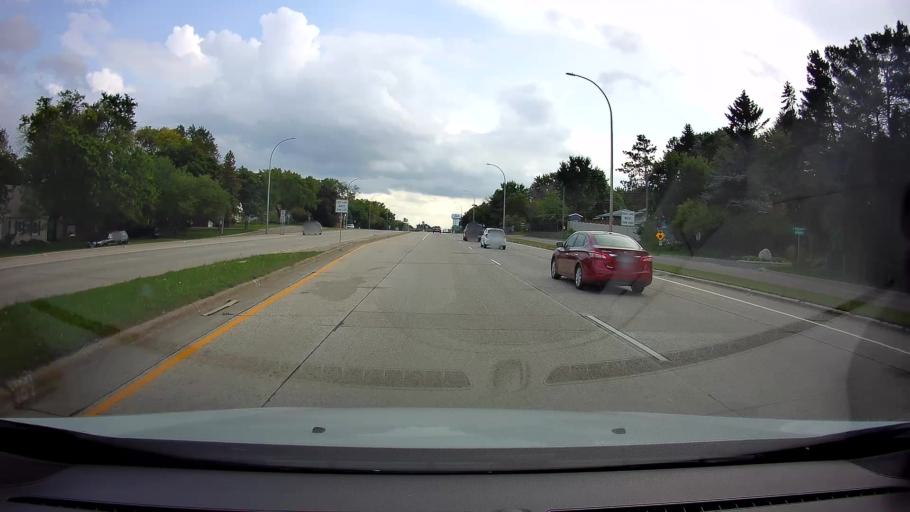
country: US
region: Minnesota
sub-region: Ramsey County
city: Falcon Heights
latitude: 44.9968
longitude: -93.1667
